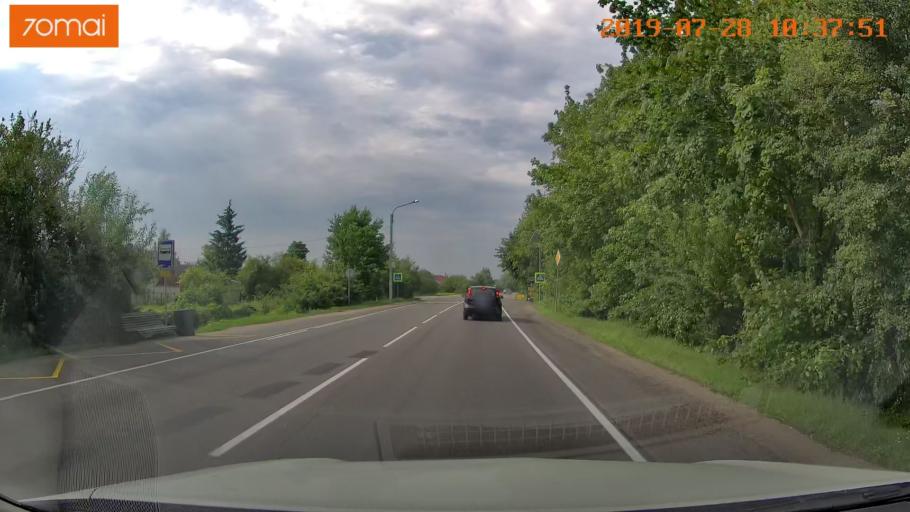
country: RU
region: Kaliningrad
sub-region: Gorod Kaliningrad
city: Kaliningrad
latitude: 54.7278
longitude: 20.4049
